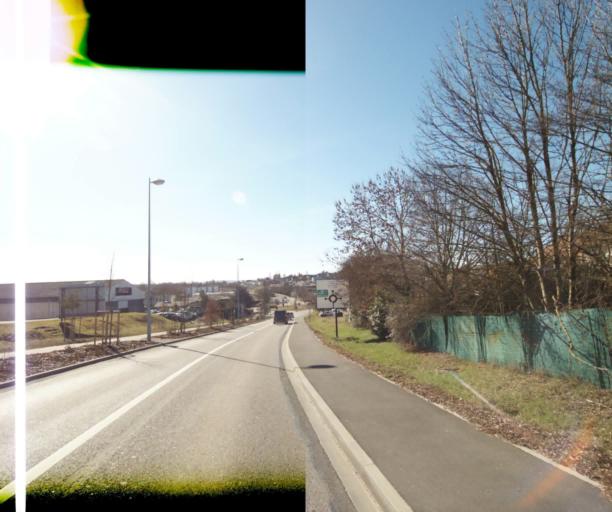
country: FR
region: Lorraine
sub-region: Departement de Meurthe-et-Moselle
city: Ludres
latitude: 48.6203
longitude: 6.1779
